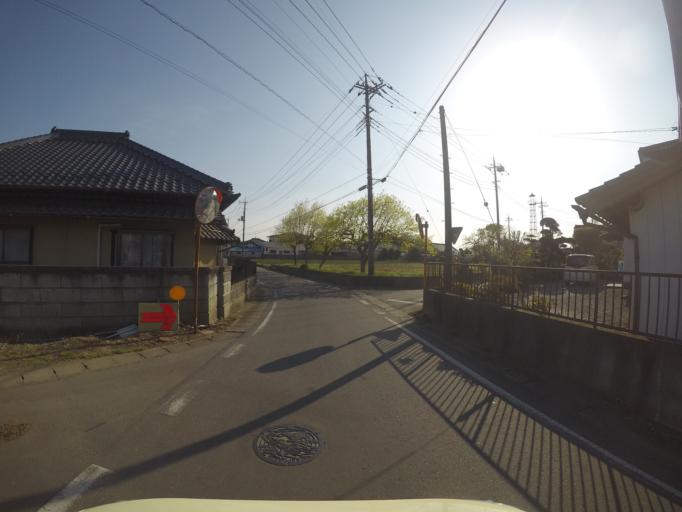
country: JP
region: Ibaraki
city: Ishige
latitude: 36.1658
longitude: 140.0159
